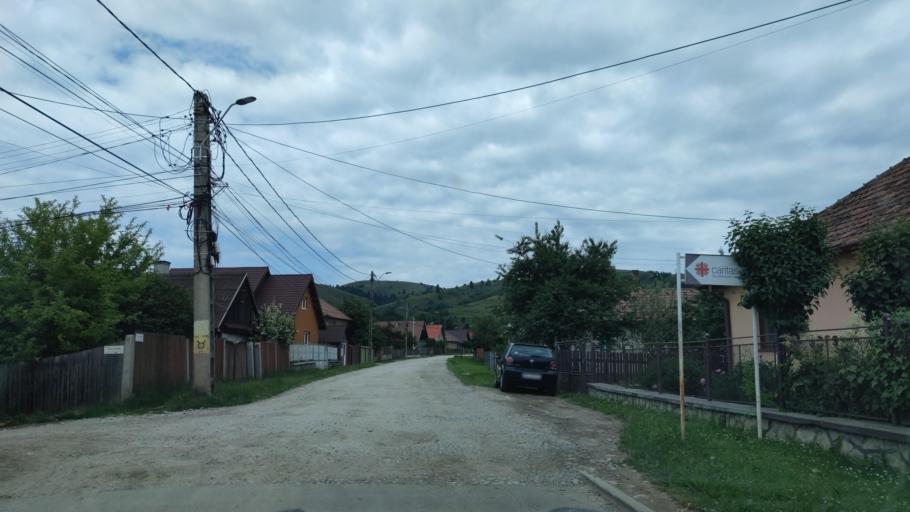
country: RO
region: Harghita
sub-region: Municipiul Gheorgheni
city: Gheorgheni
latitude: 46.7282
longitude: 25.6087
